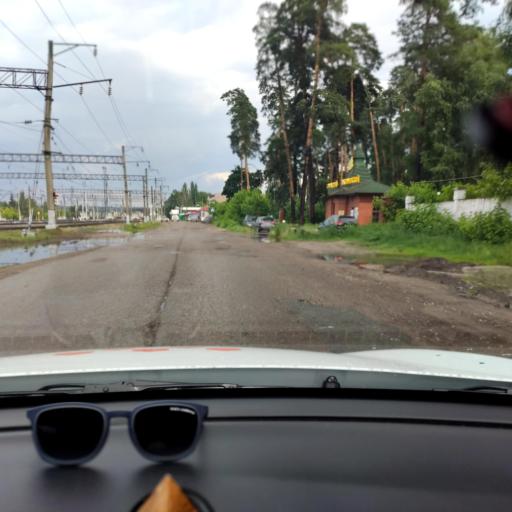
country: RU
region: Tatarstan
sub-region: Zelenodol'skiy Rayon
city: Vasil'yevo
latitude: 55.8369
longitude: 48.7004
